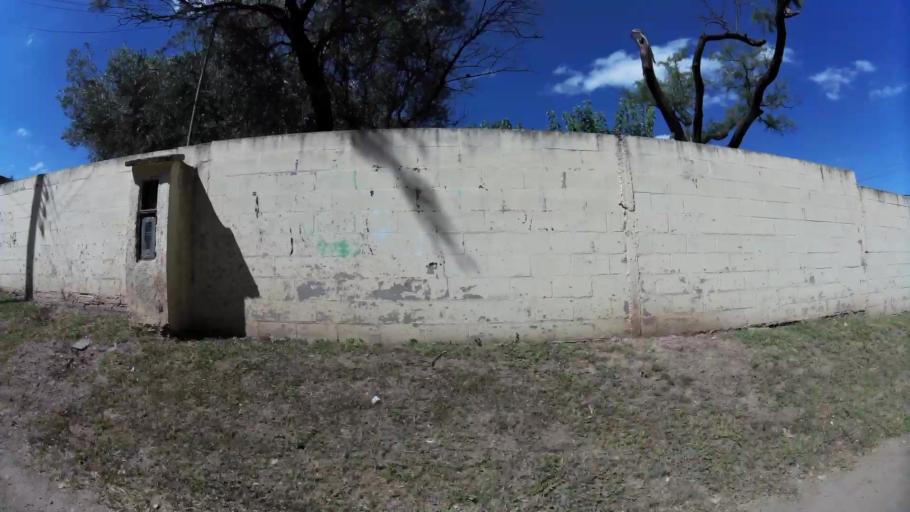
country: AR
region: Cordoba
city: Saldan
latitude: -31.2984
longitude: -64.3046
